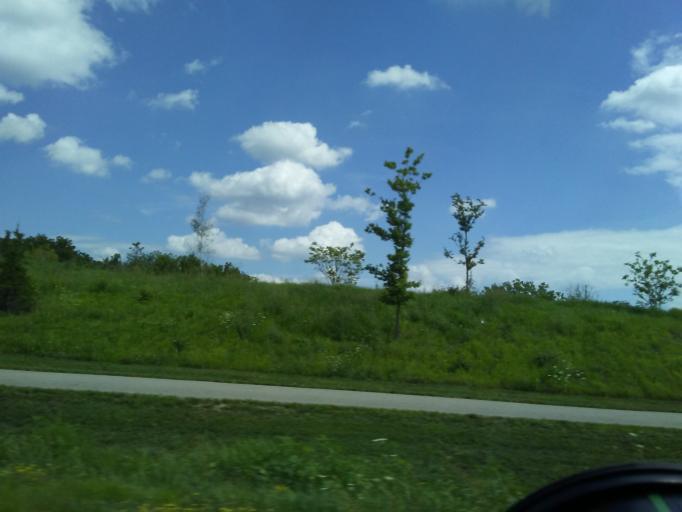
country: US
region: Wisconsin
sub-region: Dane County
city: Verona
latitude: 42.9985
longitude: -89.5577
